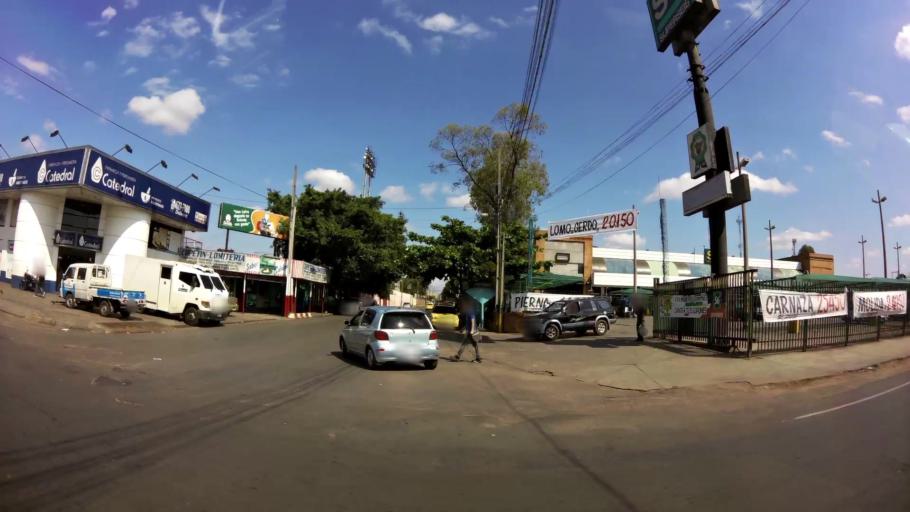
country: PY
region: Central
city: San Lorenzo
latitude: -25.3424
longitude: -57.5018
